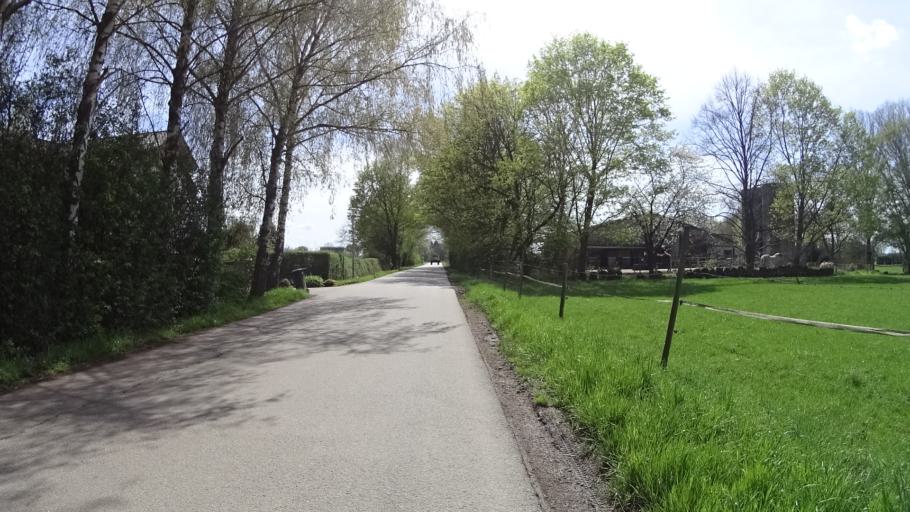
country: DE
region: Baden-Wuerttemberg
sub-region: Karlsruhe Region
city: Hemsbach
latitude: 49.5970
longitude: 8.6171
